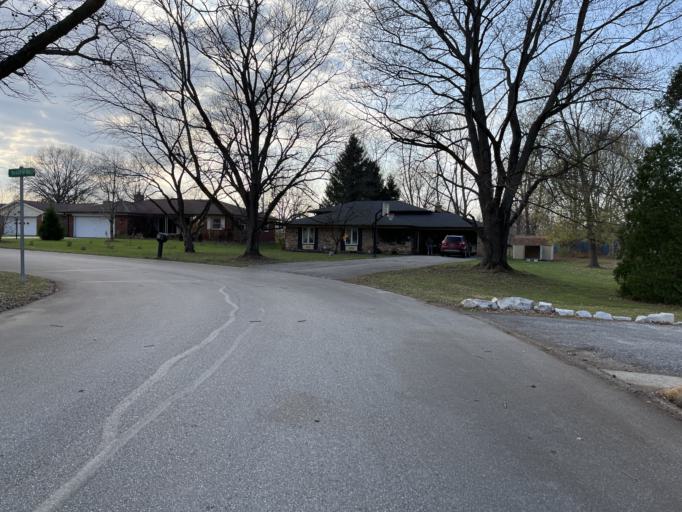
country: US
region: Indiana
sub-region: Hendricks County
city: Avon
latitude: 39.7665
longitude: -86.3980
